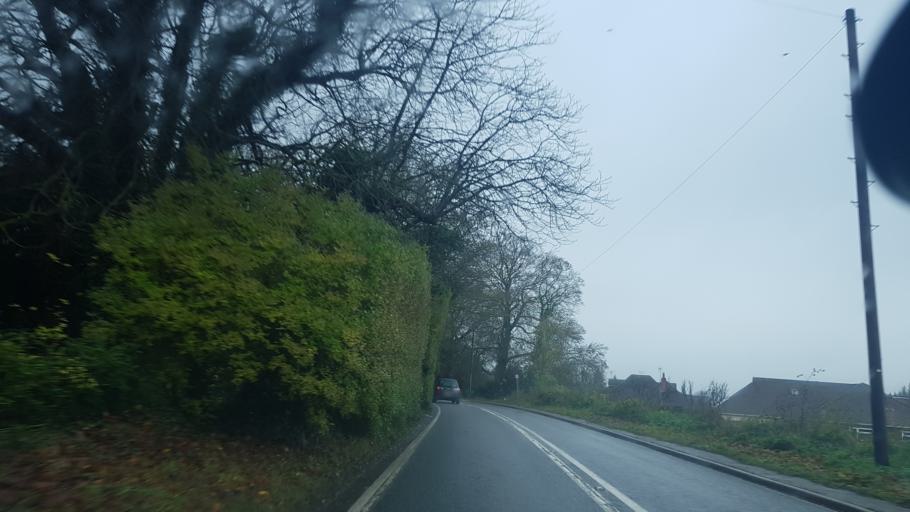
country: GB
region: England
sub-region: Surrey
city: East Horsley
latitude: 51.2655
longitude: -0.4049
